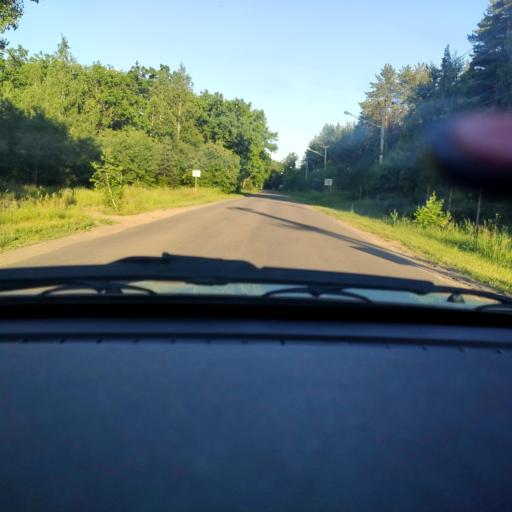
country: RU
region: Voronezj
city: Ramon'
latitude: 51.8954
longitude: 39.2773
